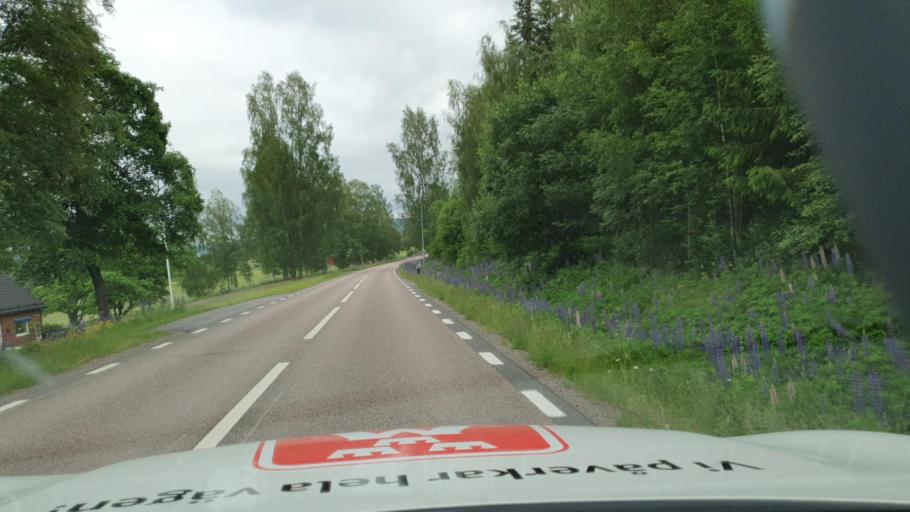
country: SE
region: Vaermland
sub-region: Sunne Kommun
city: Sunne
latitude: 59.8689
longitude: 12.9423
